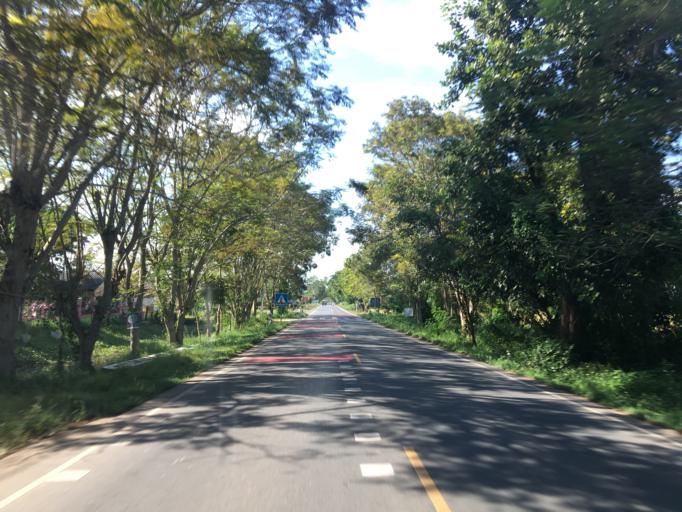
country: TH
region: Phayao
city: Chun
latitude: 19.3267
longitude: 100.1446
